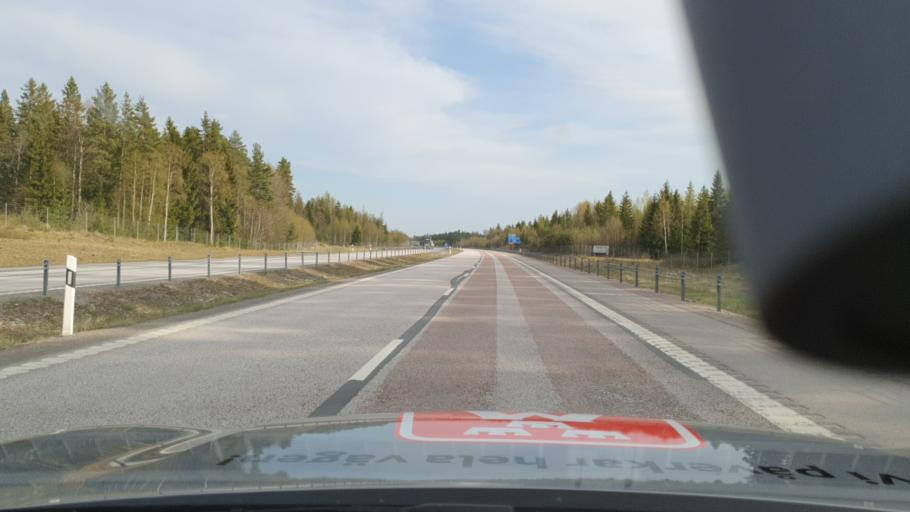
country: SE
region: Uppsala
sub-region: Tierps Kommun
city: Tierp
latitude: 60.1830
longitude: 17.5027
